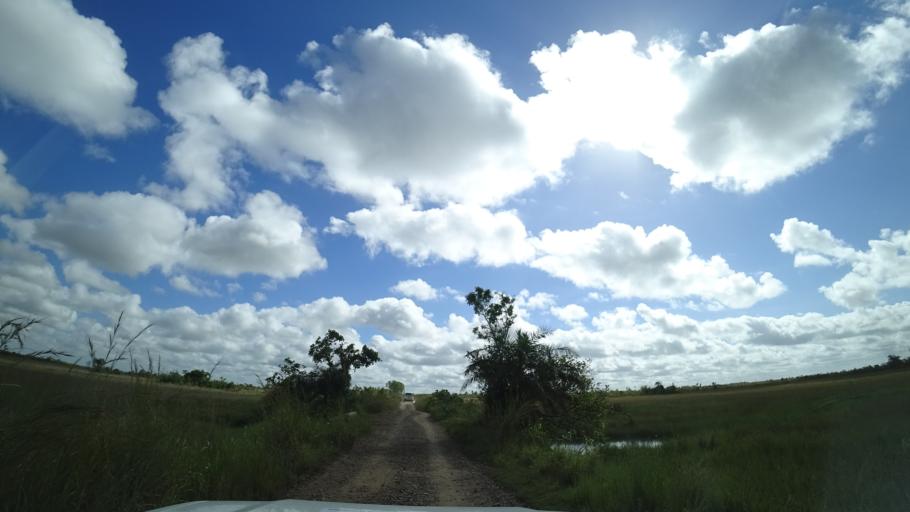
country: MZ
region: Sofala
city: Beira
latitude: -19.6272
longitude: 35.0602
